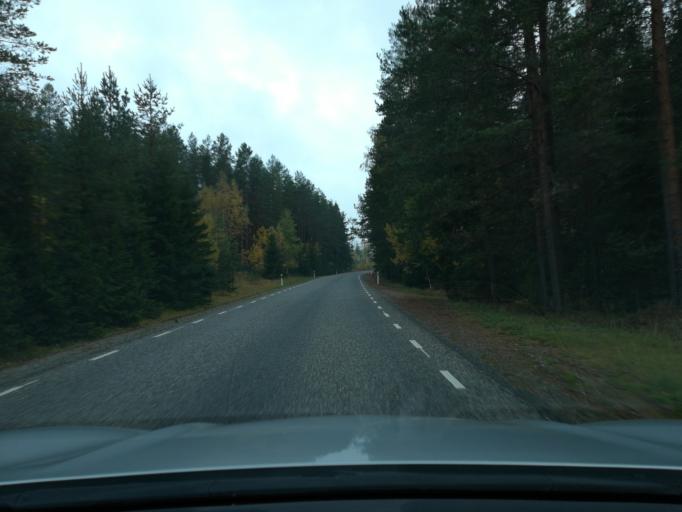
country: EE
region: Ida-Virumaa
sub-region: Johvi vald
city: Johvi
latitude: 59.1703
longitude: 27.4481
